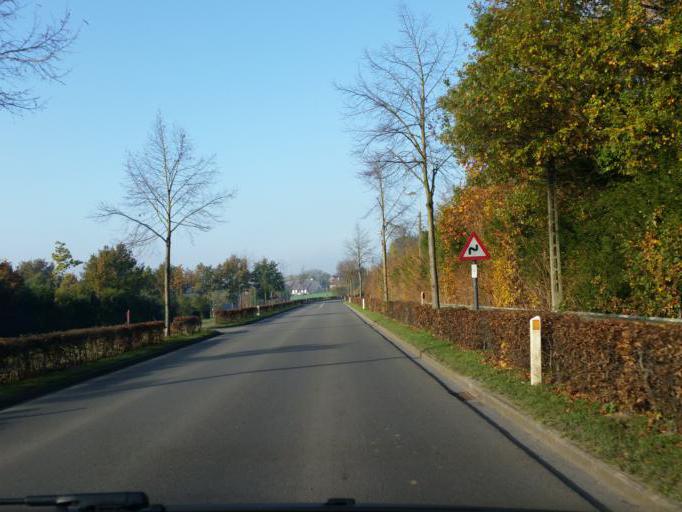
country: BE
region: Flanders
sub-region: Provincie Oost-Vlaanderen
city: Lebbeke
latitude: 50.9458
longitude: 4.1056
